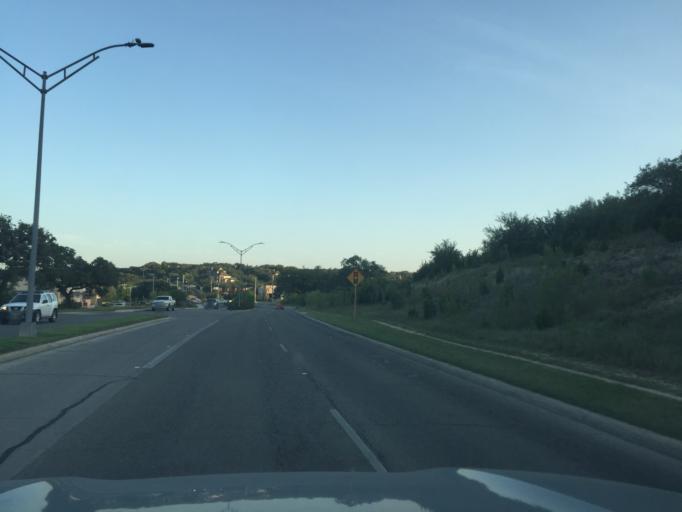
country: US
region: Texas
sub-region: Bexar County
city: Hollywood Park
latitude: 29.6454
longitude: -98.4811
